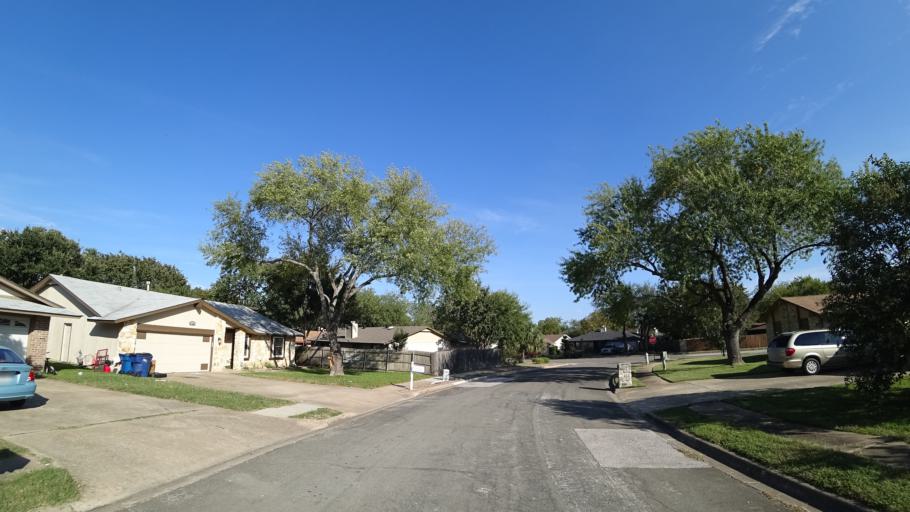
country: US
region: Texas
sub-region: Williamson County
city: Anderson Mill
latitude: 30.4566
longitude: -97.8135
